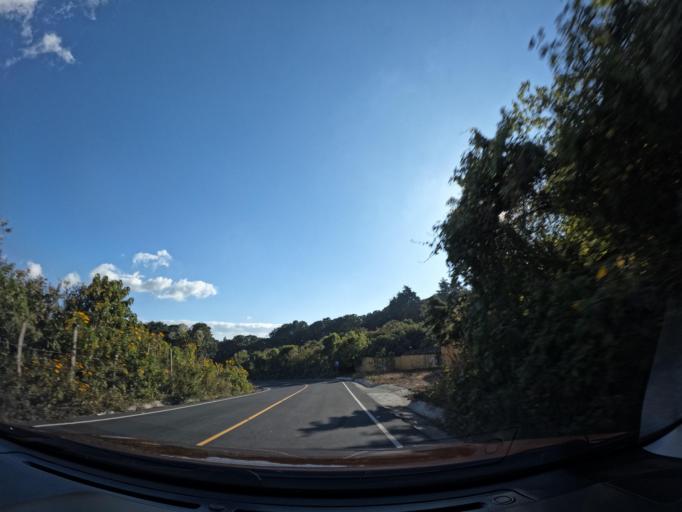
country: GT
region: Escuintla
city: Palin
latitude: 14.4622
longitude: -90.6943
